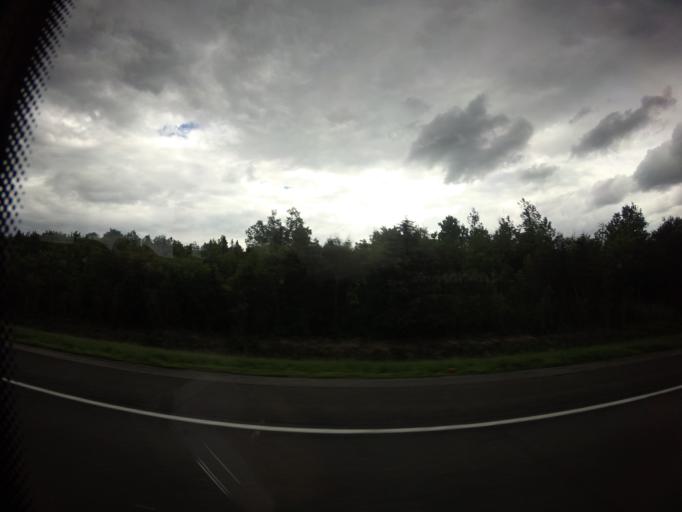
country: CA
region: Quebec
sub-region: Capitale-Nationale
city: Donnacona
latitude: 46.5042
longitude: -71.6712
